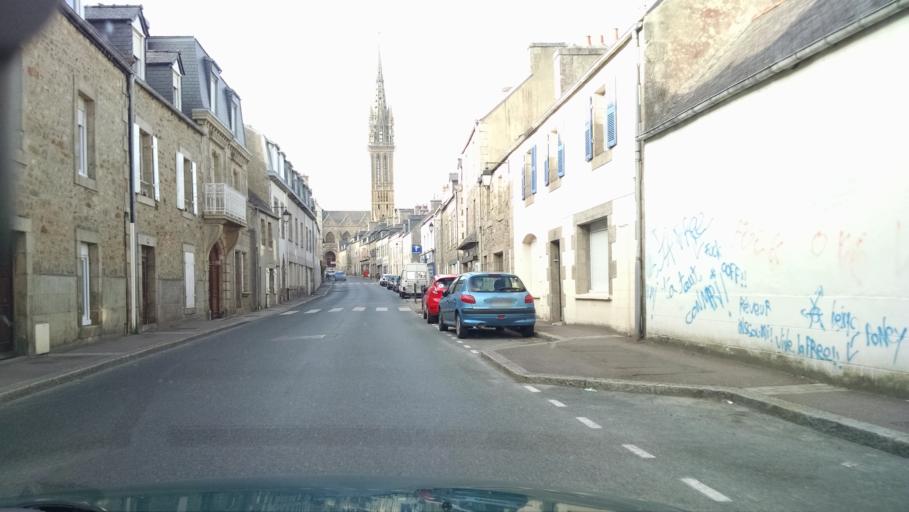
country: FR
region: Brittany
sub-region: Departement du Finistere
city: Saint-Pol-de-Leon
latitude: 48.6807
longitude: -3.9876
